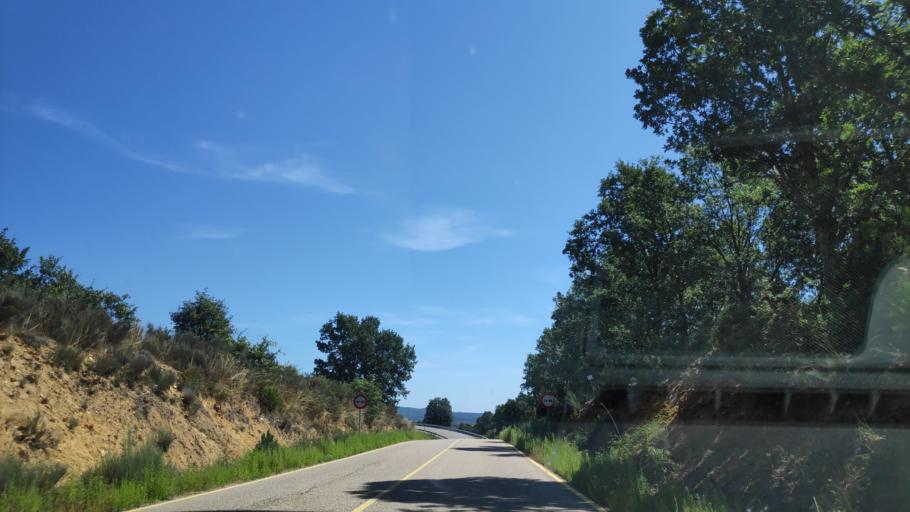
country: ES
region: Castille and Leon
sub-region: Provincia de Zamora
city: Puebla de Sanabria
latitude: 42.0437
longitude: -6.6562
